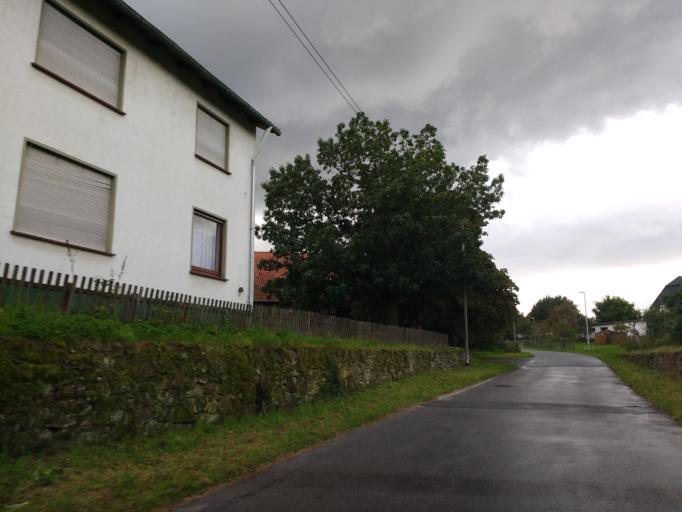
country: DE
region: North Rhine-Westphalia
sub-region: Regierungsbezirk Detmold
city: Bad Meinberg
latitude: 51.9191
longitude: 9.0349
